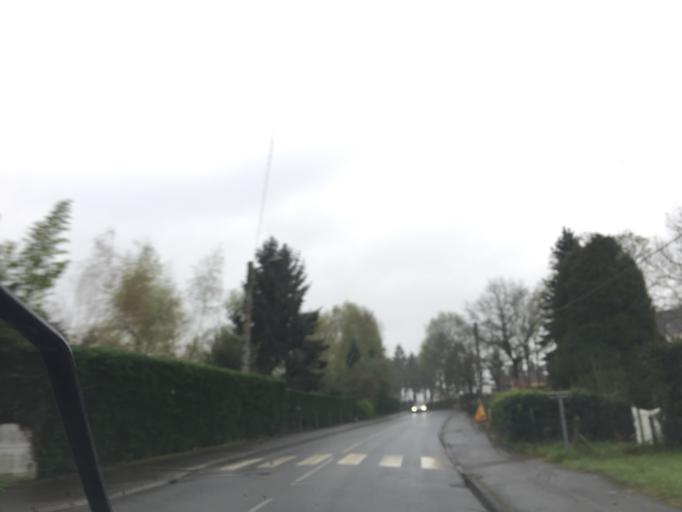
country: FR
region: Pays de la Loire
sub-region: Departement de la Loire-Atlantique
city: Suce-sur-Erdre
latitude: 47.3485
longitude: -1.5306
